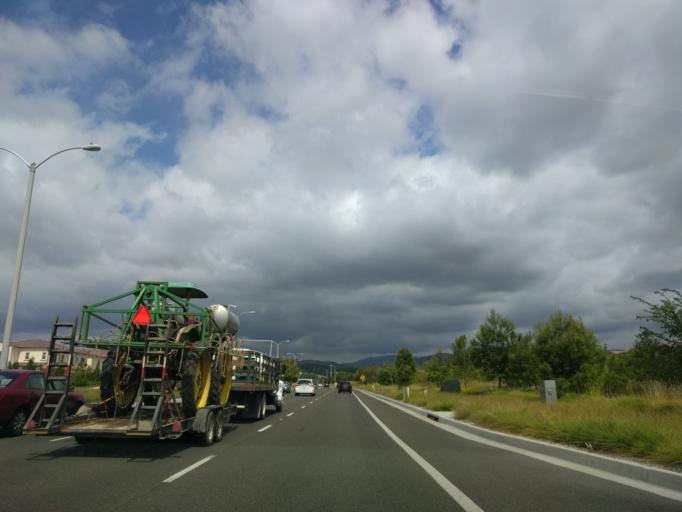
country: US
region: California
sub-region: Orange County
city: North Tustin
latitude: 33.7079
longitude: -117.7503
